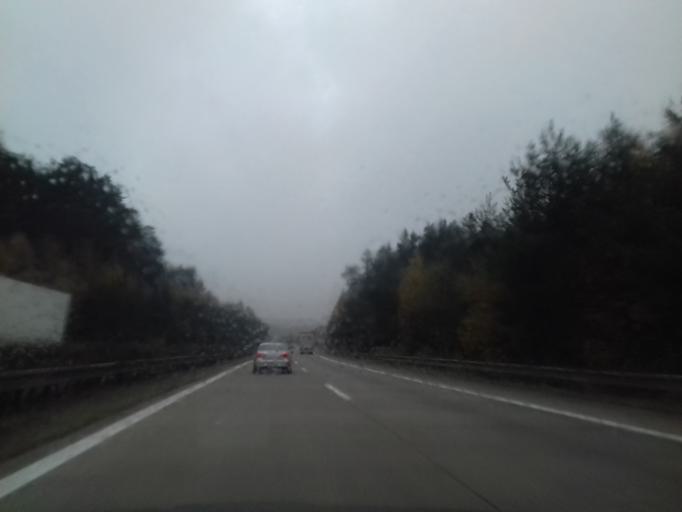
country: CZ
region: Vysocina
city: Heralec
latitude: 49.5101
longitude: 15.4634
